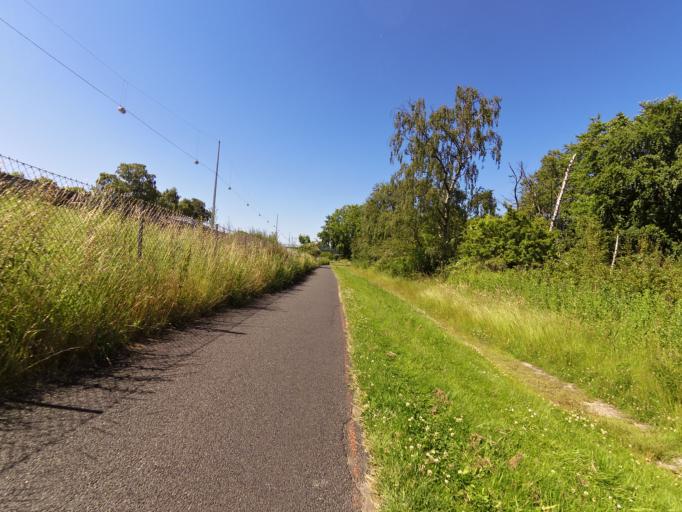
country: DK
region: Capital Region
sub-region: Gladsaxe Municipality
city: Buddinge
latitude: 55.7239
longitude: 12.4895
